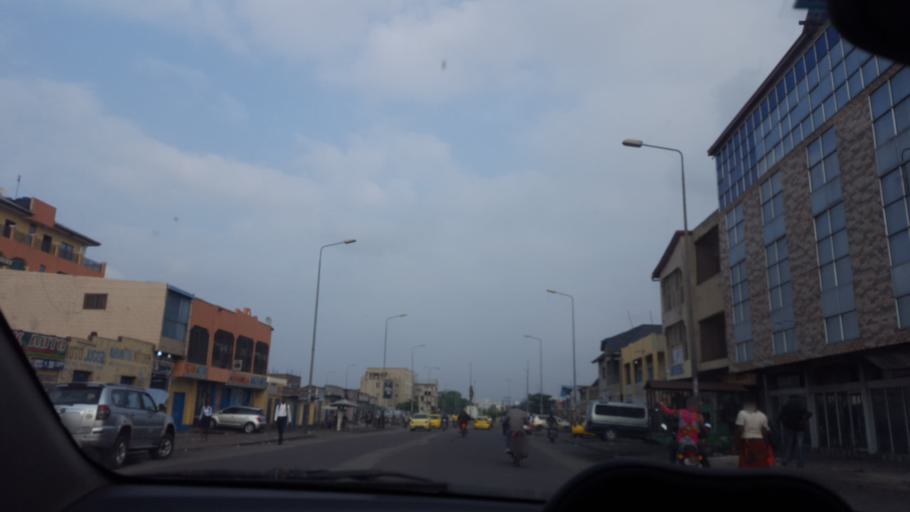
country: CD
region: Kinshasa
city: Kinshasa
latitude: -4.3386
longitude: 15.3066
